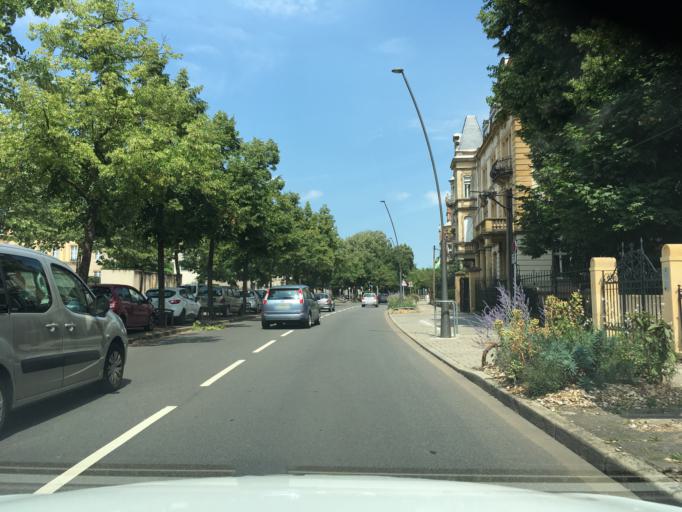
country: FR
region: Lorraine
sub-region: Departement de la Moselle
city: Metz
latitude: 49.1212
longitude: 6.1834
